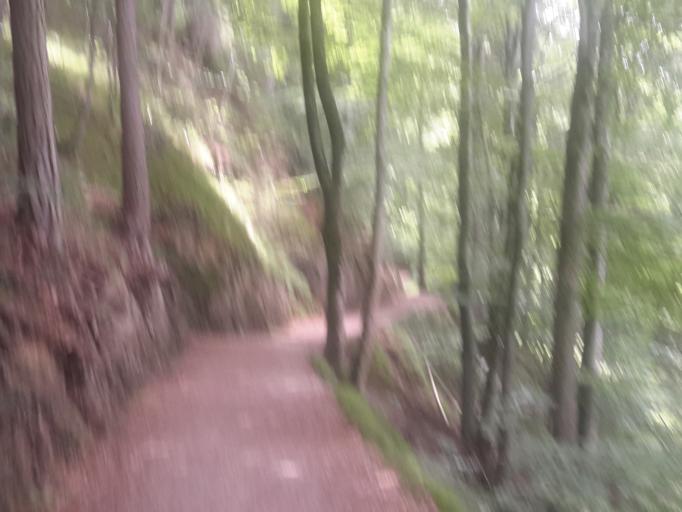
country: DE
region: Bavaria
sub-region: Upper Bavaria
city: Kiefersfelden
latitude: 47.6095
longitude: 12.1671
